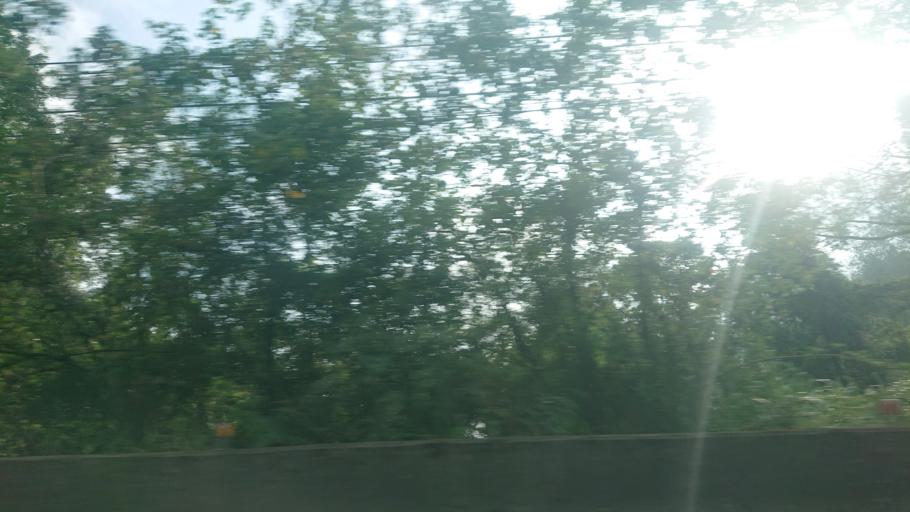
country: TW
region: Taiwan
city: Lugu
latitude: 23.4972
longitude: 120.7880
